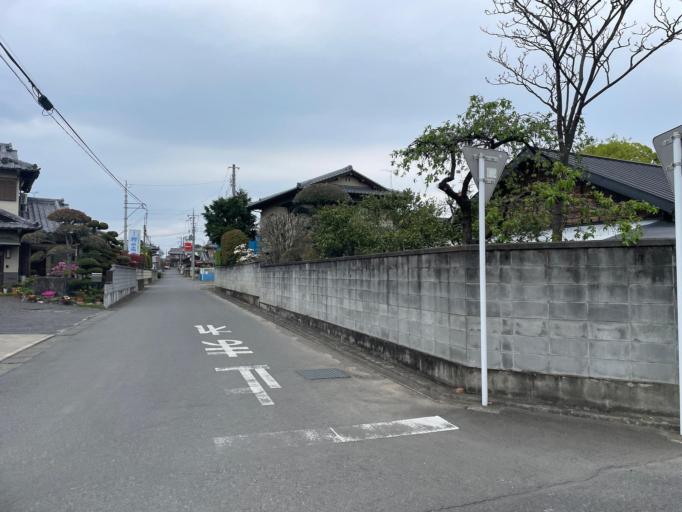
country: JP
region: Gunma
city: Sakai-nakajima
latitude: 36.2745
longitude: 139.2421
